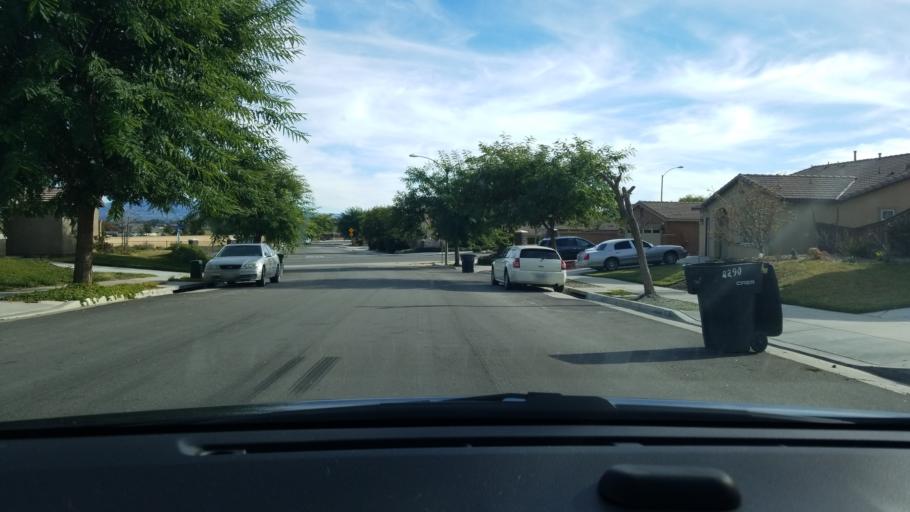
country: US
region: California
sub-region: Riverside County
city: Green Acres
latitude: 33.7978
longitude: -117.0367
